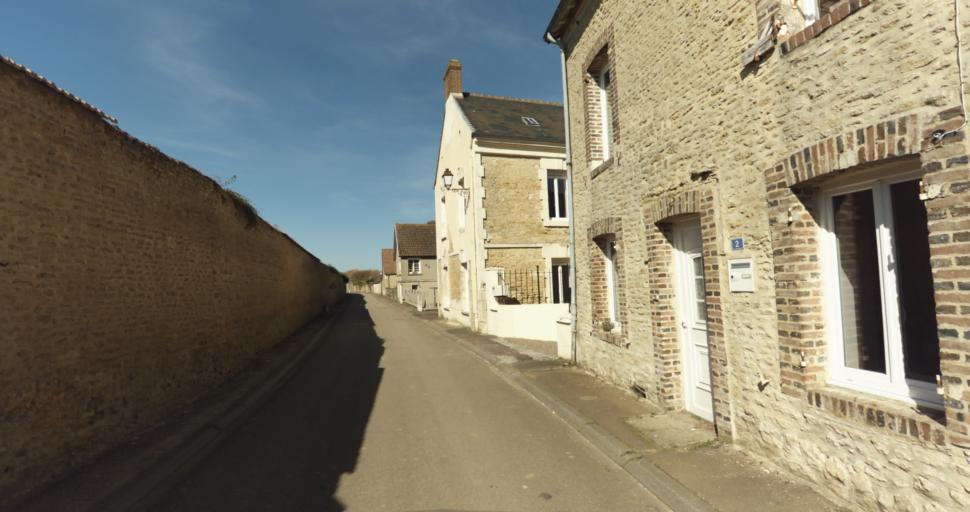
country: FR
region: Lower Normandy
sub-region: Departement du Calvados
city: Saint-Pierre-sur-Dives
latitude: 49.0384
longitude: -0.0261
